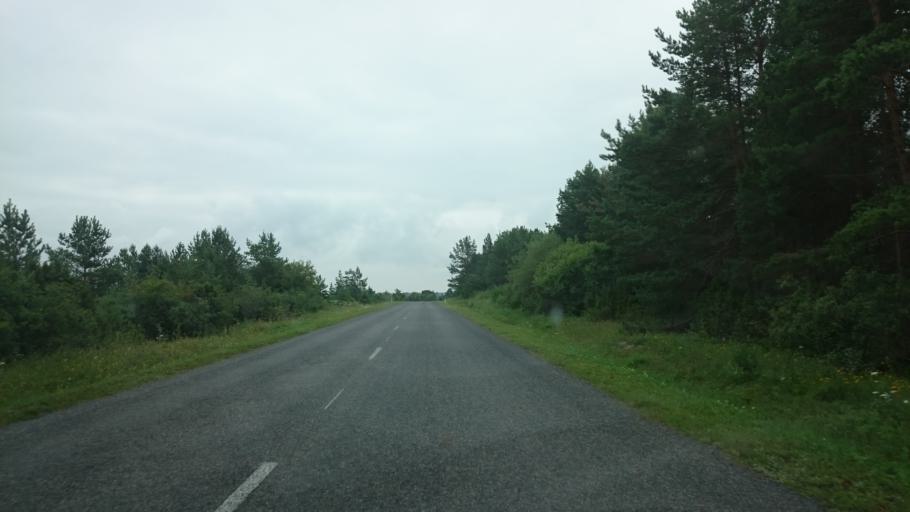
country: EE
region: Saare
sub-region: Orissaare vald
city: Orissaare
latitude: 58.5867
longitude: 23.0223
